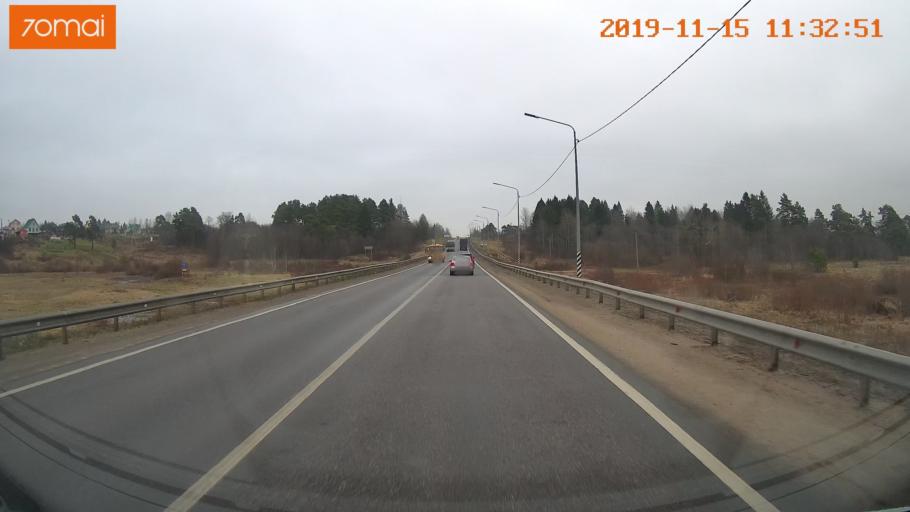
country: RU
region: Vologda
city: Molochnoye
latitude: 59.1872
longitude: 39.5821
